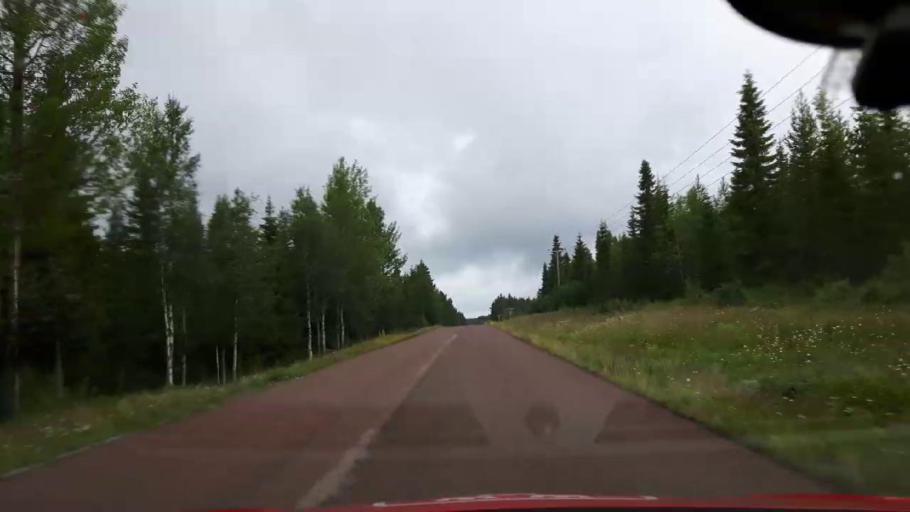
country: SE
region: Jaemtland
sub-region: Krokoms Kommun
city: Valla
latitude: 63.3411
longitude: 13.7174
